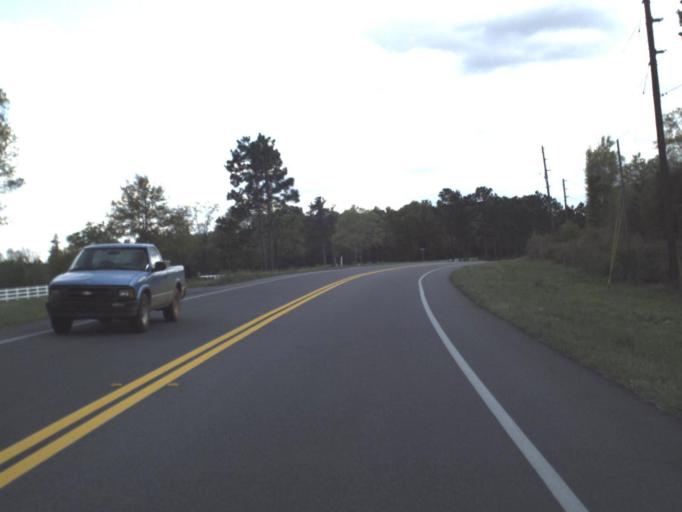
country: US
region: Florida
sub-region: Okaloosa County
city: Crestview
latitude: 30.8833
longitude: -86.5071
